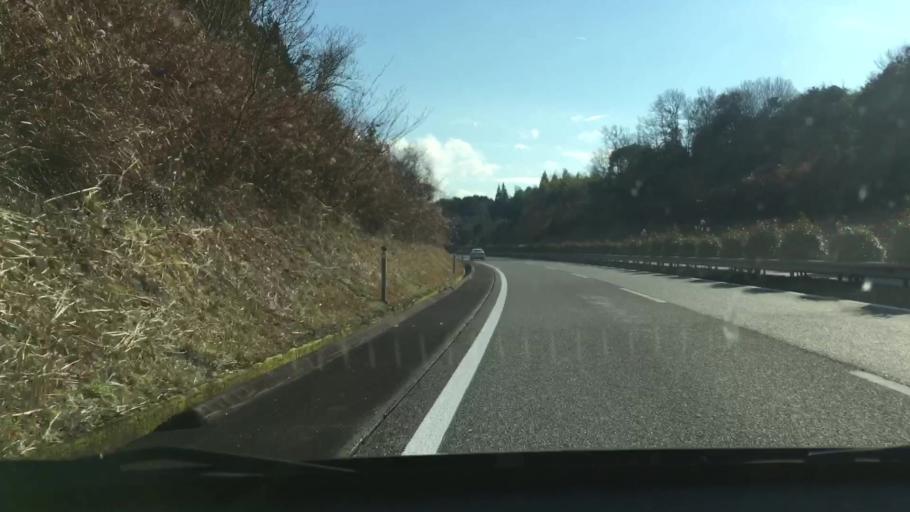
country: JP
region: Kumamoto
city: Hitoyoshi
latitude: 32.1901
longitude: 130.7769
